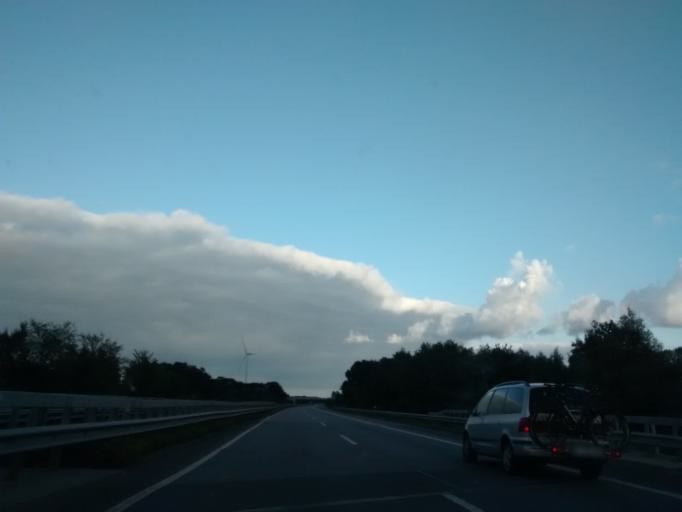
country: DE
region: Lower Saxony
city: Quendorf
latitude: 52.3433
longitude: 7.1870
